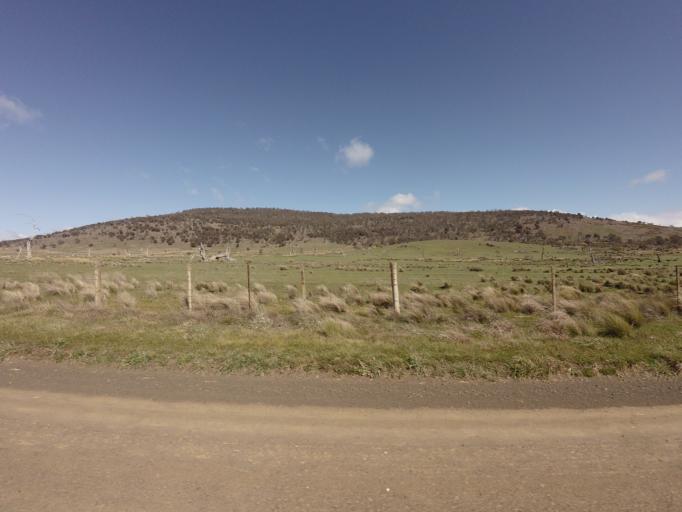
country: AU
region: Tasmania
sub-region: Northern Midlands
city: Evandale
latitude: -41.9240
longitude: 147.4062
